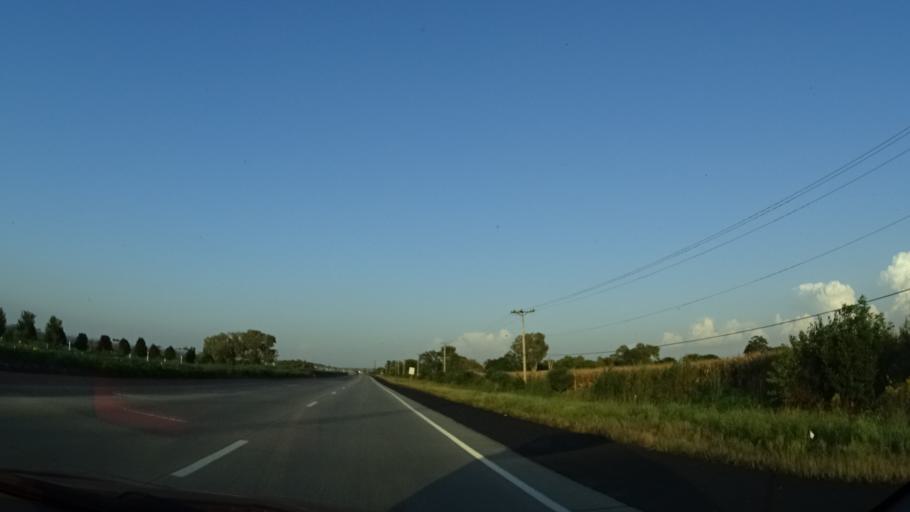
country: US
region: Iowa
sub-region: Pottawattamie County
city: Council Bluffs
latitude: 41.2151
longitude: -95.8887
